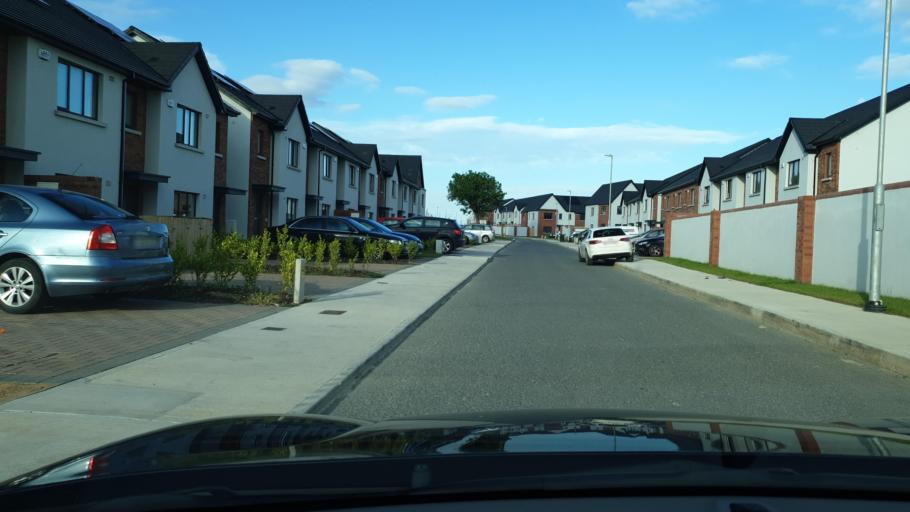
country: IE
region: Leinster
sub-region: Fingal County
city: Blanchardstown
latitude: 53.4230
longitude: -6.3701
